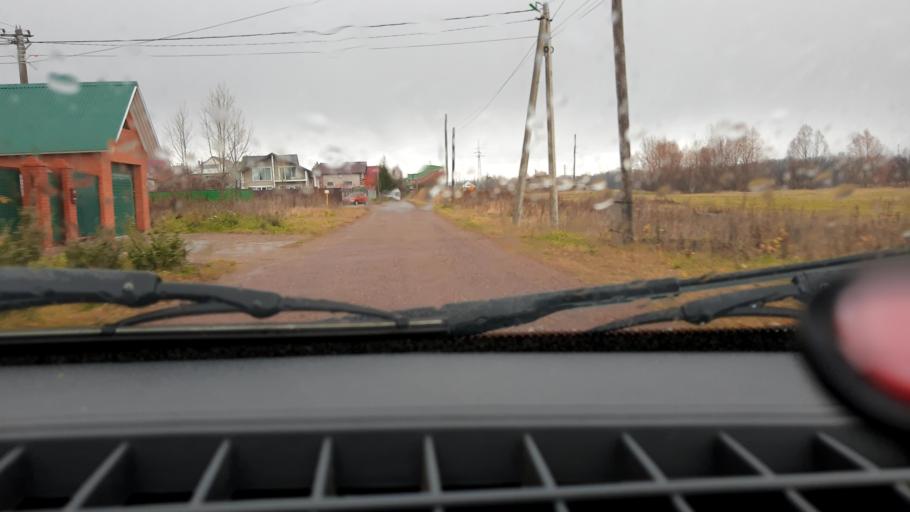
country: RU
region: Bashkortostan
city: Ufa
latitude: 54.8208
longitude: 55.9922
